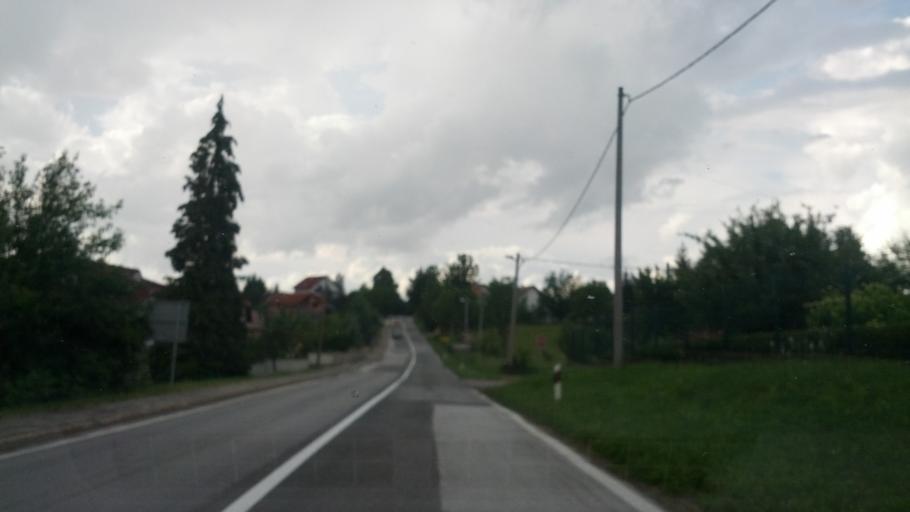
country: HR
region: Licko-Senjska
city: Jezerce
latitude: 44.9513
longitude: 15.6729
